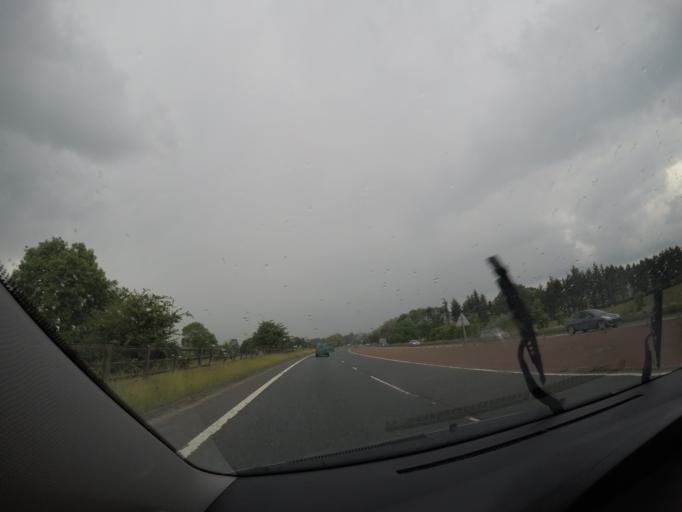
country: GB
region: England
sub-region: Cumbria
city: Penrith
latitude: 54.6542
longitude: -2.7119
